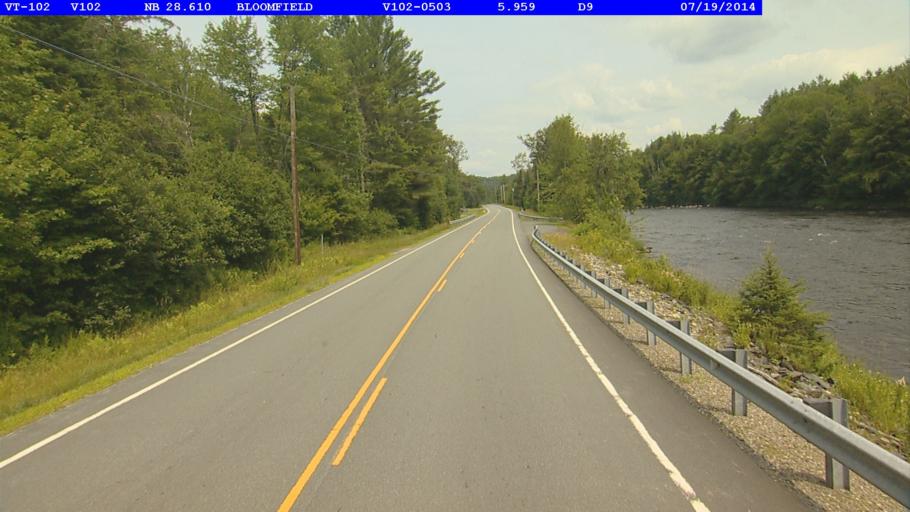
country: US
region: New Hampshire
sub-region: Coos County
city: Colebrook
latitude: 44.8156
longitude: -71.5772
